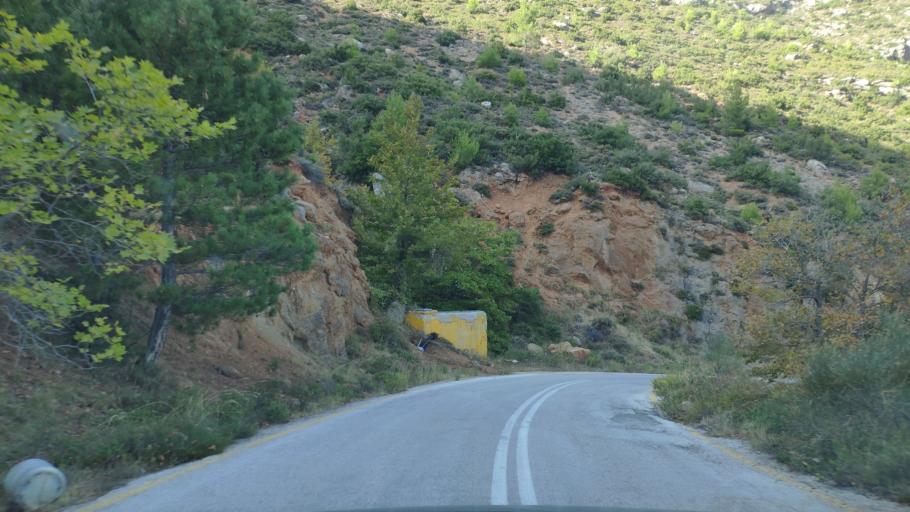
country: GR
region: West Greece
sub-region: Nomos Achaias
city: Aiyira
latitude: 38.0675
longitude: 22.3791
